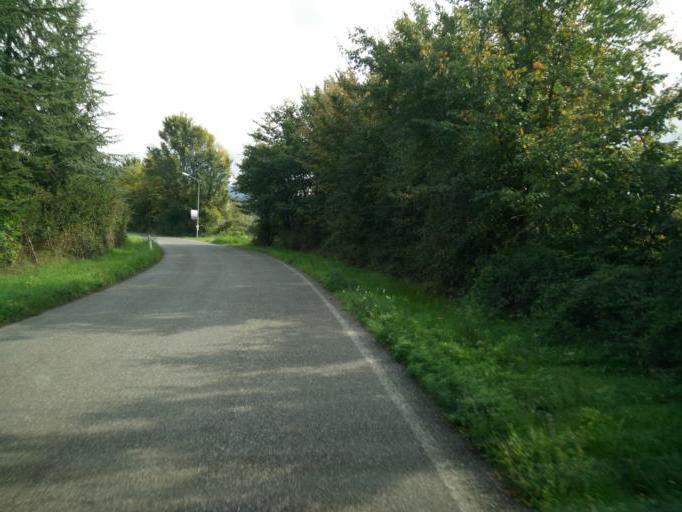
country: IT
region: Tuscany
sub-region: Provincia di Massa-Carrara
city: Villafranca in Lunigiana
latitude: 44.3130
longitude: 9.9532
